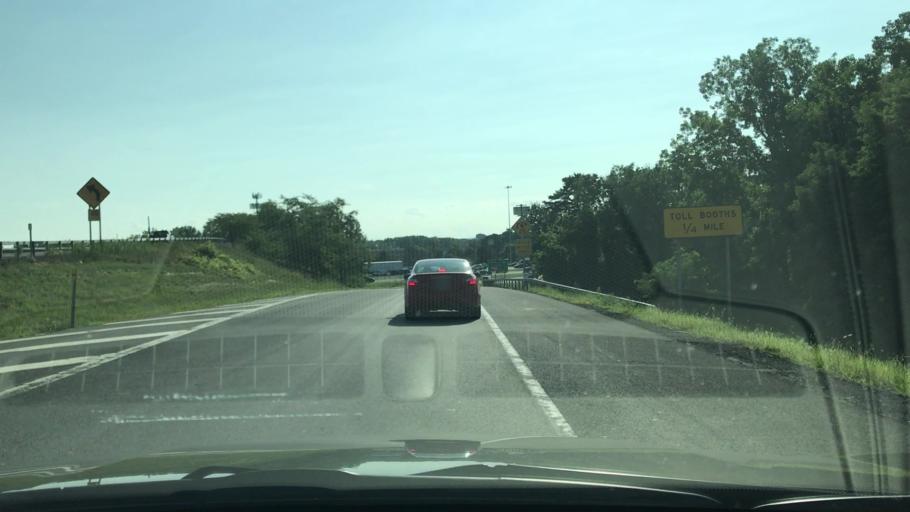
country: US
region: New York
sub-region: Albany County
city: McKownville
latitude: 42.6972
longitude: -73.8391
